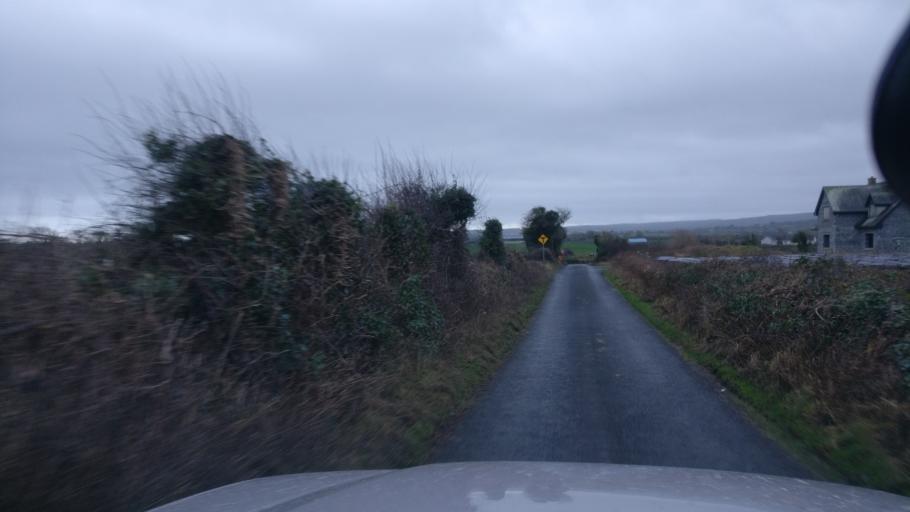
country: IE
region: Connaught
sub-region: County Galway
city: Loughrea
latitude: 53.2044
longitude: -8.6617
